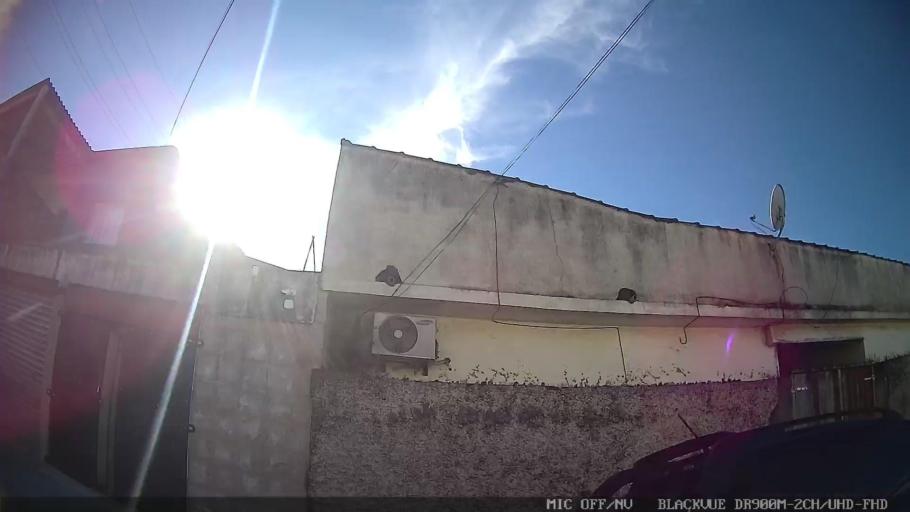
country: BR
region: Sao Paulo
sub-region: Guaruja
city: Guaruja
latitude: -23.9490
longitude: -46.2820
